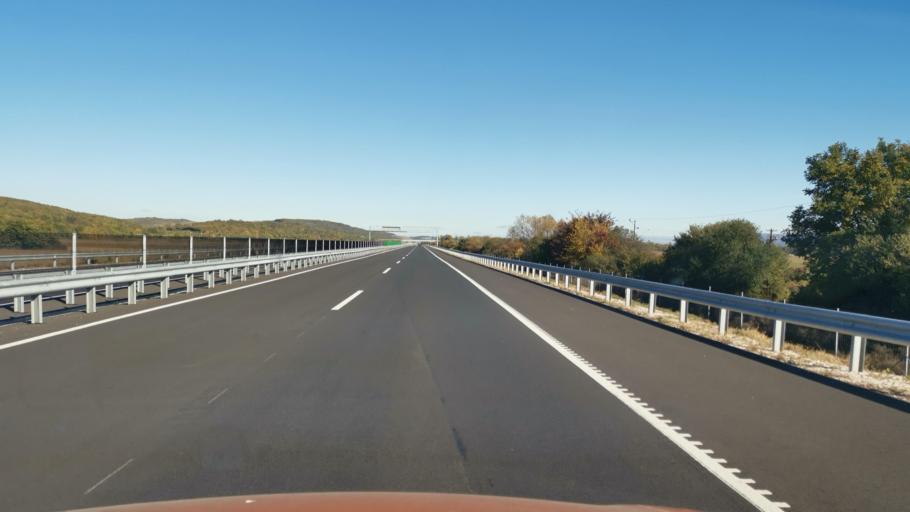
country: HU
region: Borsod-Abauj-Zemplen
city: Gonc
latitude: 48.4351
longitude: 21.1882
